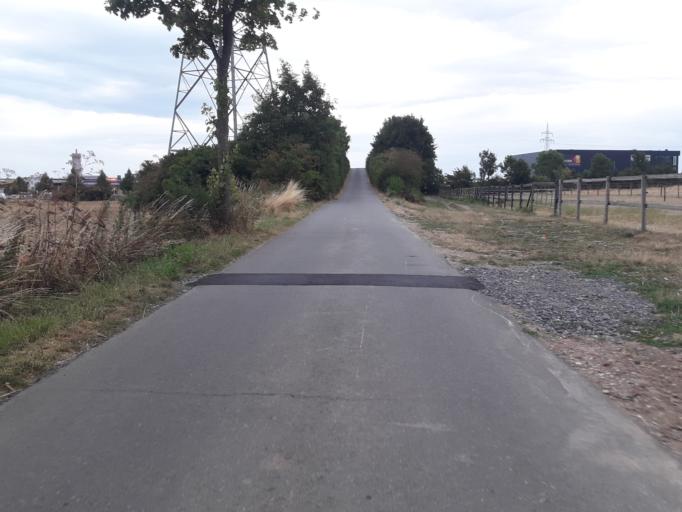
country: DE
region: North Rhine-Westphalia
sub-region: Regierungsbezirk Detmold
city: Paderborn
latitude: 51.6813
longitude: 8.7231
